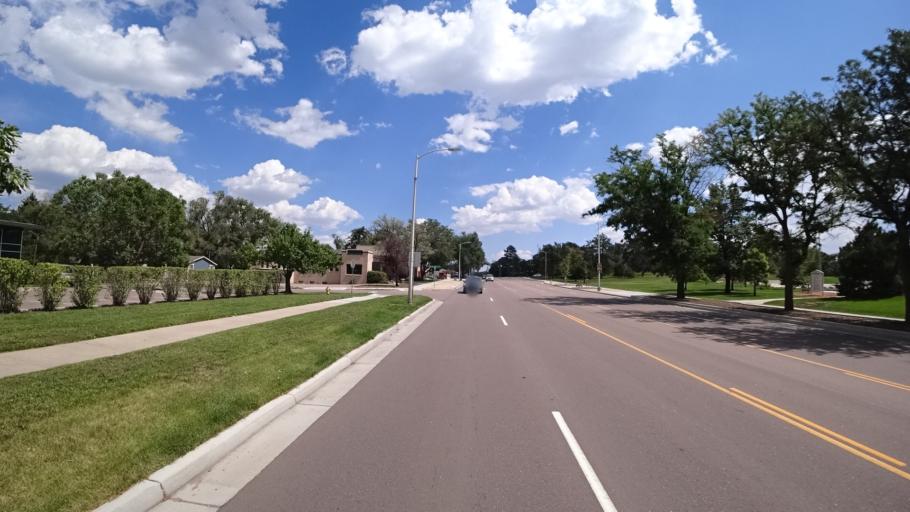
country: US
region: Colorado
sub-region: El Paso County
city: Colorado Springs
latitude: 38.8331
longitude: -104.7966
